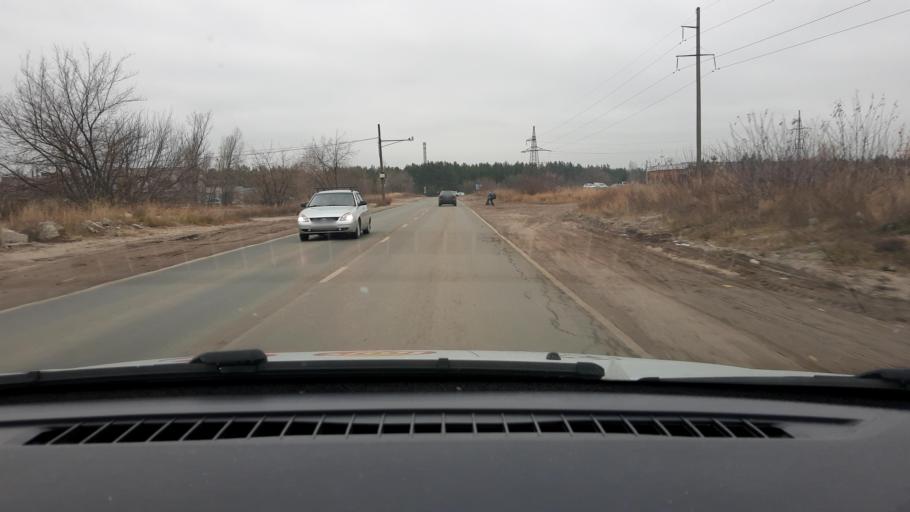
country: RU
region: Nizjnij Novgorod
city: Dzerzhinsk
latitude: 56.2497
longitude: 43.4208
